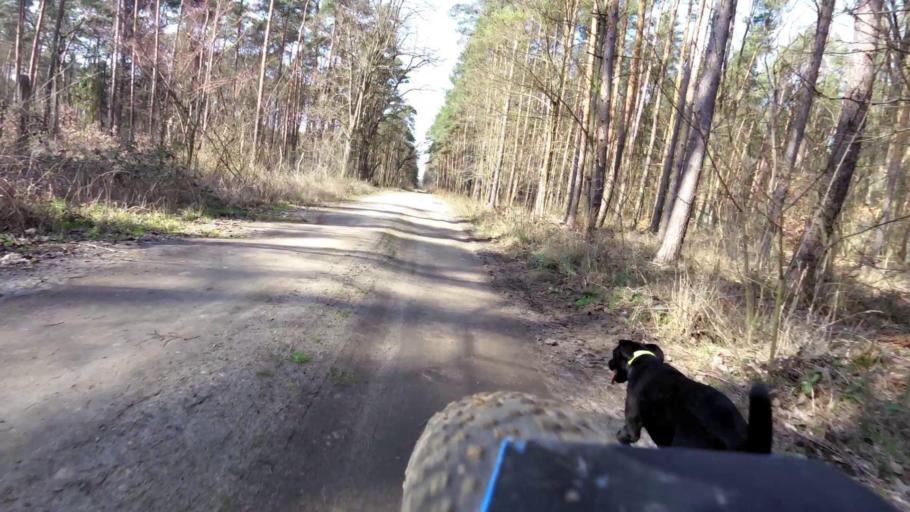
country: PL
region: Lubusz
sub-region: Powiat slubicki
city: Cybinka
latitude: 52.2117
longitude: 14.8605
